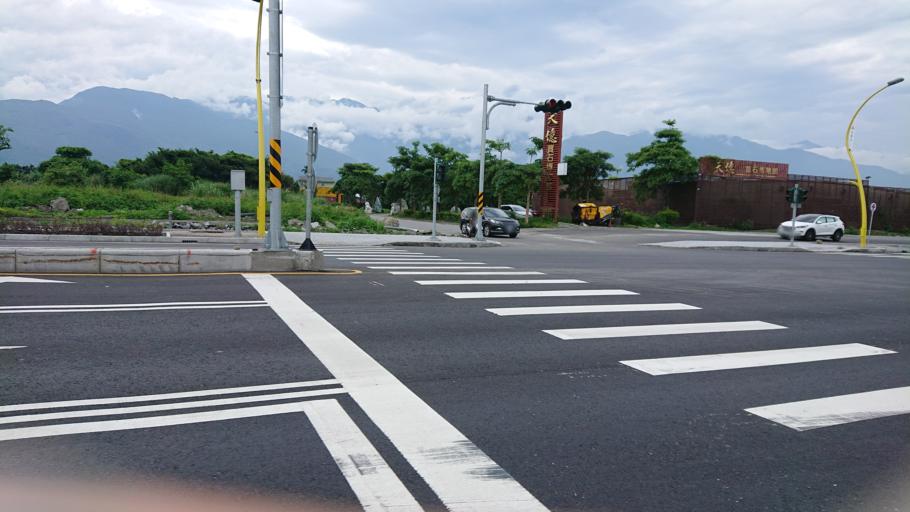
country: TW
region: Taiwan
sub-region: Hualien
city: Hualian
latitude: 23.9547
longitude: 121.6012
